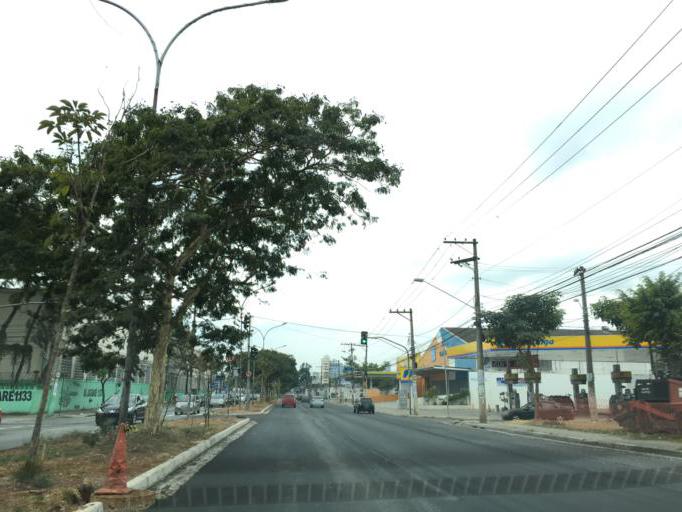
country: BR
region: Sao Paulo
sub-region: Osasco
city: Osasco
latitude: -23.5522
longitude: -46.7413
